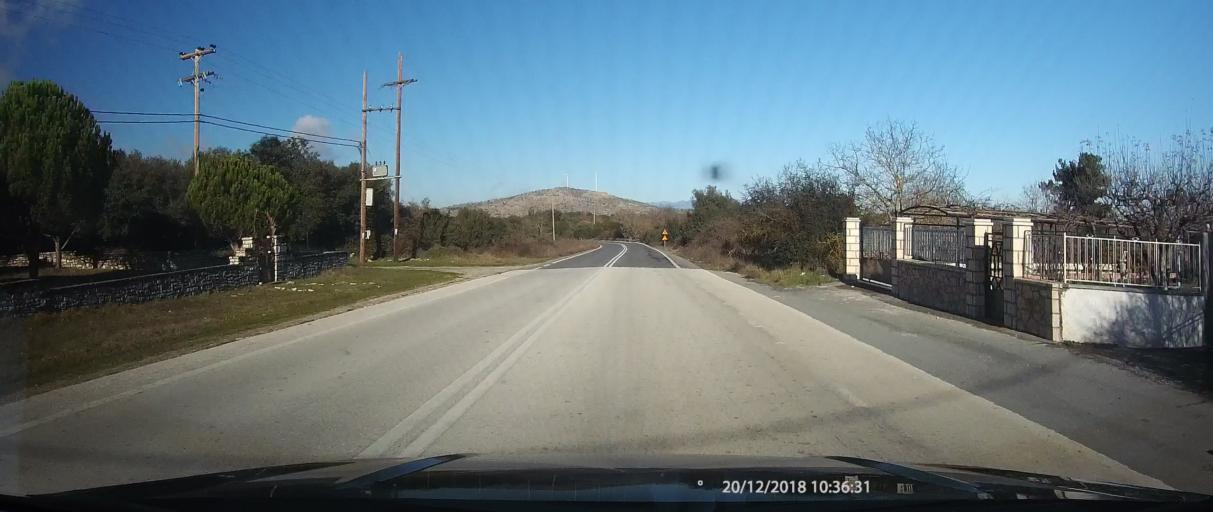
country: GR
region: Peloponnese
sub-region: Nomos Lakonias
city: Kariai
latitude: 37.3672
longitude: 22.4008
